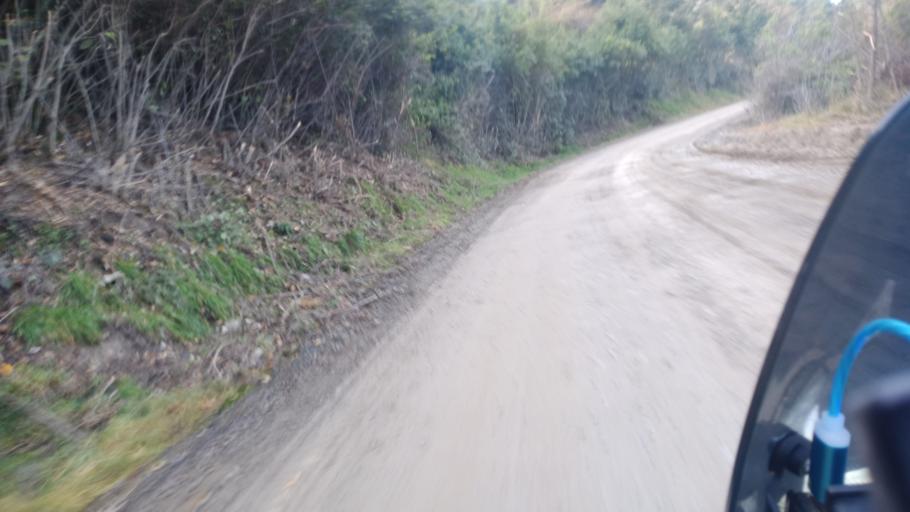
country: NZ
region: Gisborne
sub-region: Gisborne District
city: Gisborne
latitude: -38.1399
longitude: 178.1946
